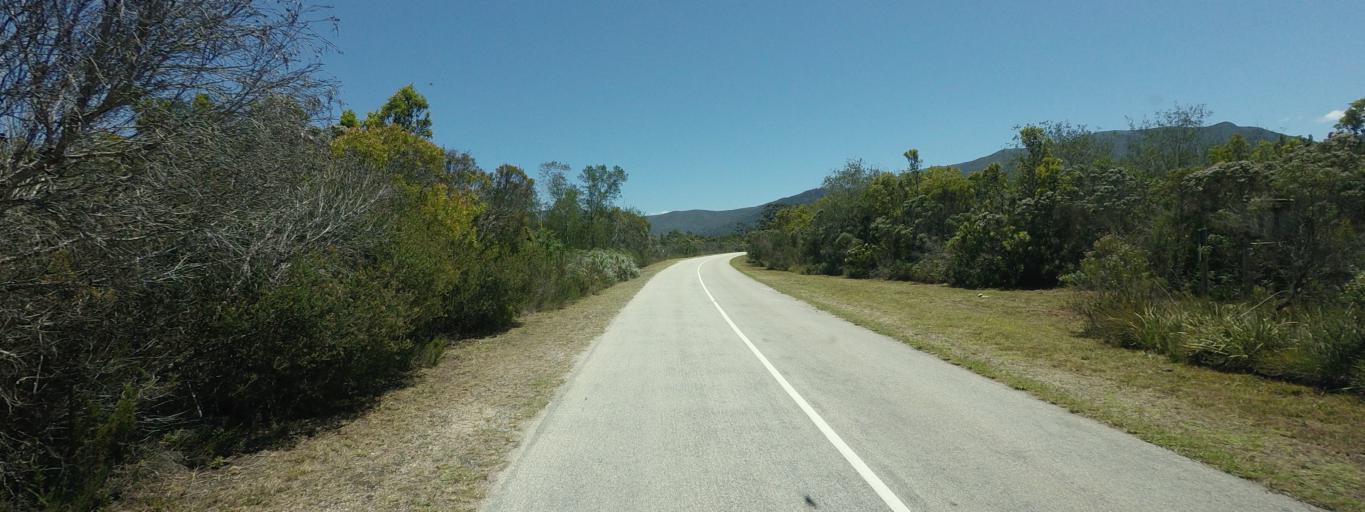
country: ZA
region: Western Cape
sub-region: Eden District Municipality
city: Plettenberg Bay
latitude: -33.9561
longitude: 23.5146
